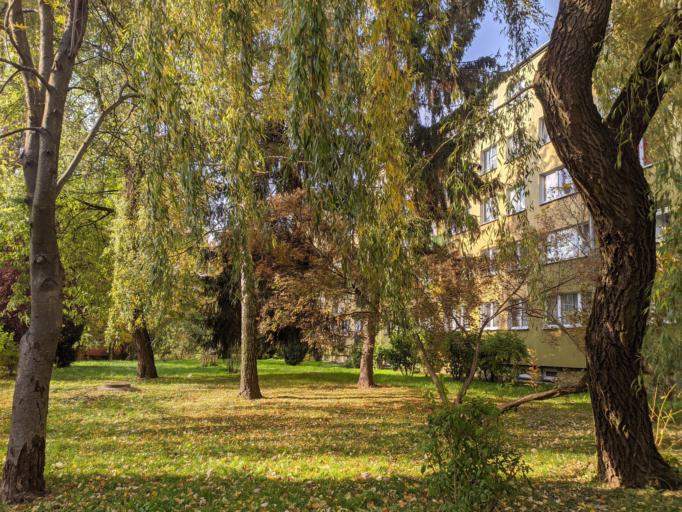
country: PL
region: Lublin Voivodeship
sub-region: Powiat lubelski
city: Lublin
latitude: 51.2399
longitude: 22.5175
